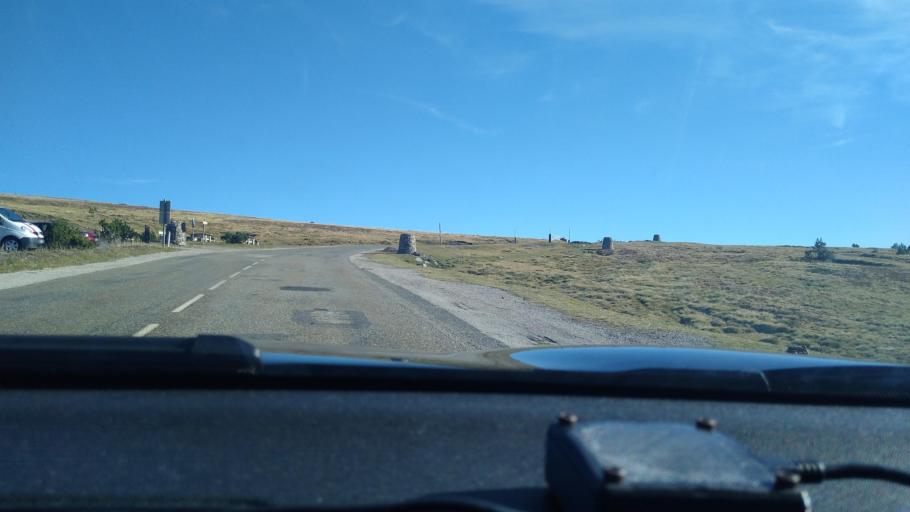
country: FR
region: Midi-Pyrenees
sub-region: Departement de l'Ariege
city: Ax-les-Thermes
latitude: 42.7330
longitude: 1.9872
